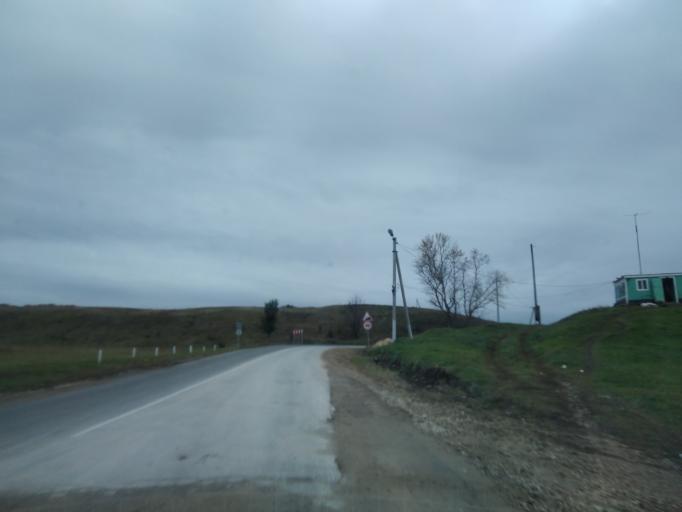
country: RU
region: Lipetsk
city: Zadonsk
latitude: 52.3202
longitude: 38.9232
